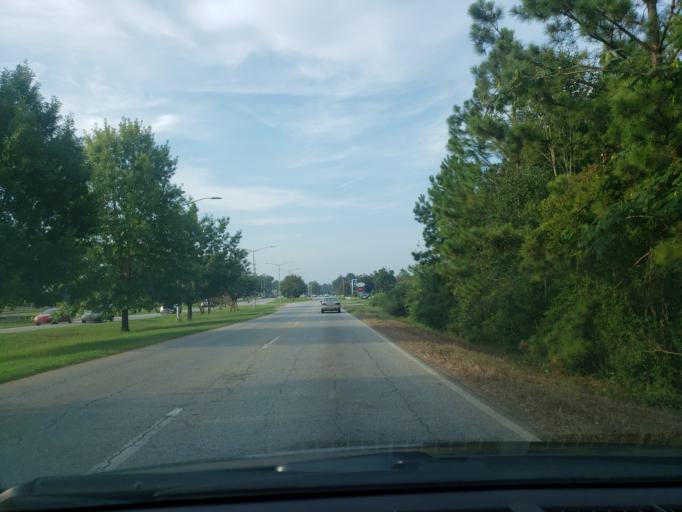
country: US
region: Georgia
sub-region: Dougherty County
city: Albany
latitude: 31.5888
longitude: -84.2196
